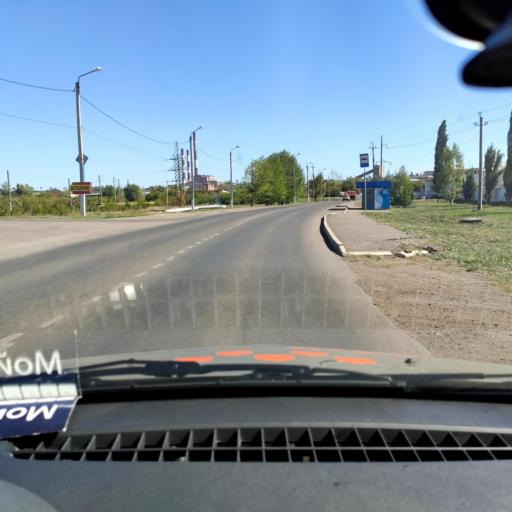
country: RU
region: Bashkortostan
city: Kumertau
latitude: 52.7718
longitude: 55.7985
